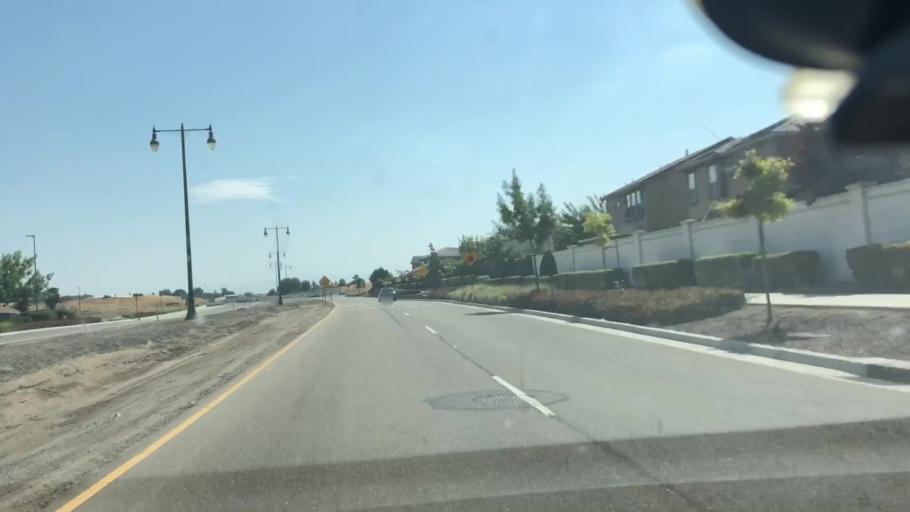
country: US
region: California
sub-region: San Joaquin County
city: Lathrop
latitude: 37.8016
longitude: -121.3019
